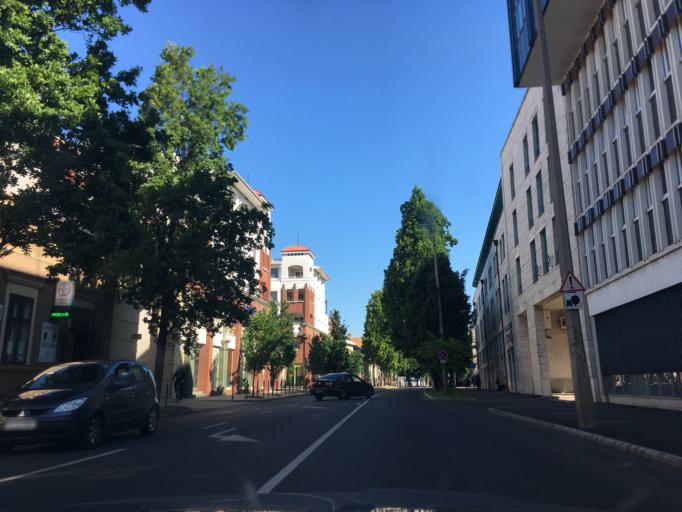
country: HU
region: Hajdu-Bihar
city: Debrecen
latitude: 47.5313
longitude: 21.6211
